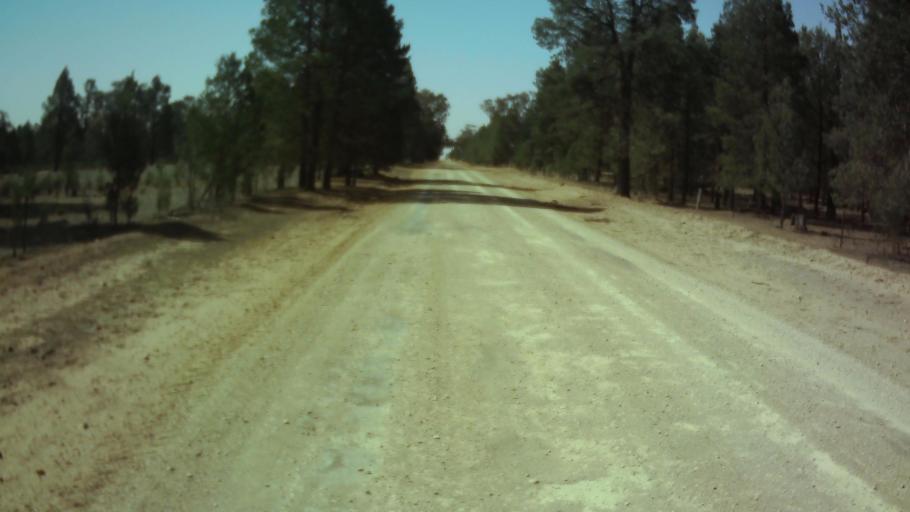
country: AU
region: New South Wales
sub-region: Weddin
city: Grenfell
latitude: -33.9638
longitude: 147.9317
